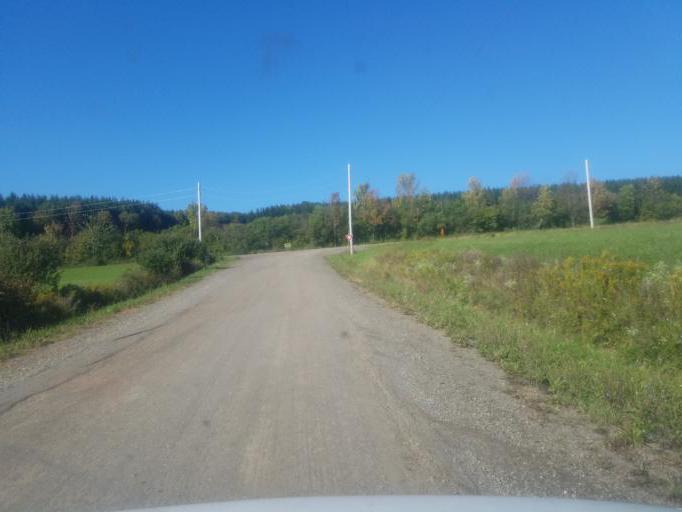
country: US
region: New York
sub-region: Allegany County
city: Cuba
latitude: 42.2382
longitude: -78.2297
